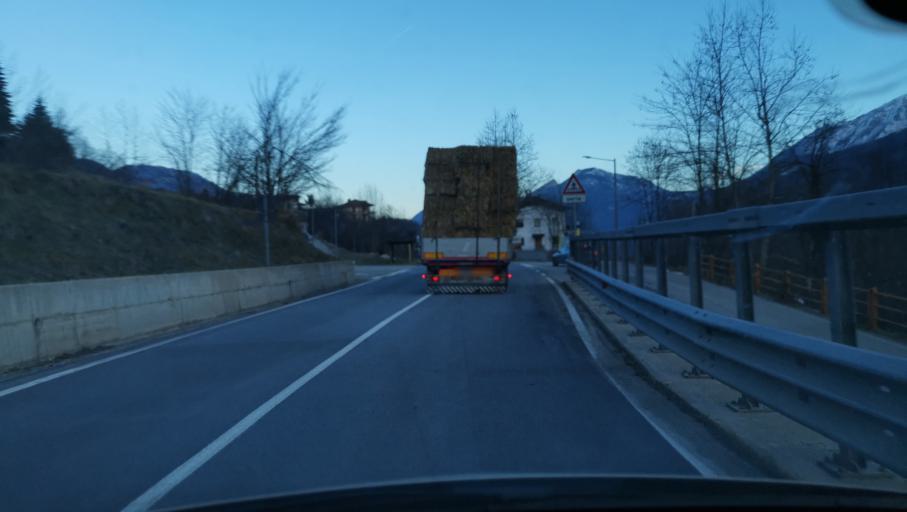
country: IT
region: Piedmont
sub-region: Provincia di Cuneo
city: Demonte
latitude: 44.3133
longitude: 7.2871
